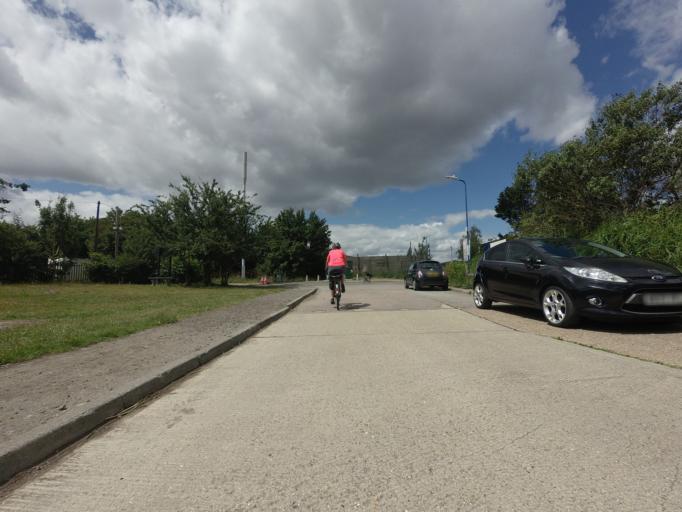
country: GB
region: England
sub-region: Kent
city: Gravesend
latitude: 51.4417
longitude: 0.3934
